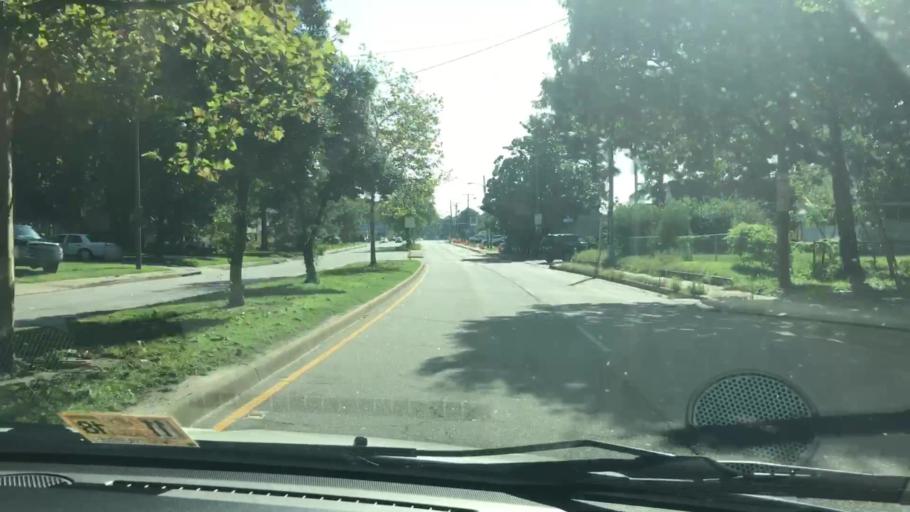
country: US
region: Virginia
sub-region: City of Norfolk
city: Norfolk
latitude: 36.8961
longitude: -76.2208
